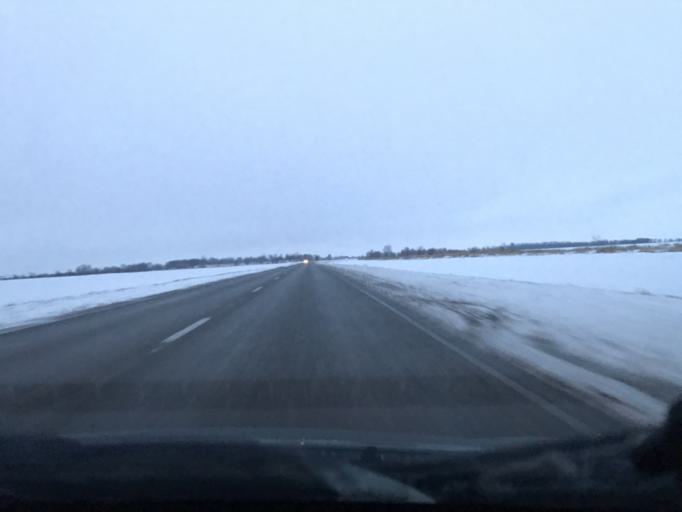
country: RU
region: Rostov
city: Letnik
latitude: 45.9490
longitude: 41.2845
